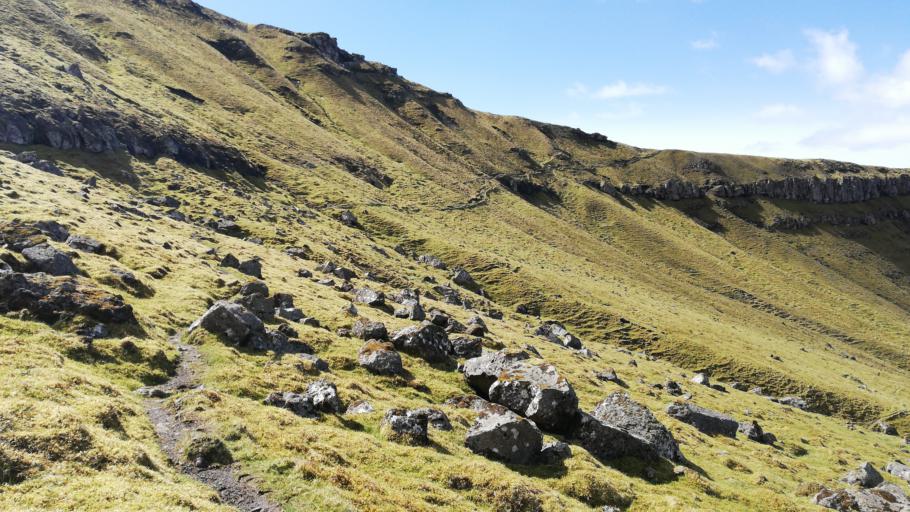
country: FO
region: Streymoy
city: Kollafjordhur
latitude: 62.0695
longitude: -6.9758
